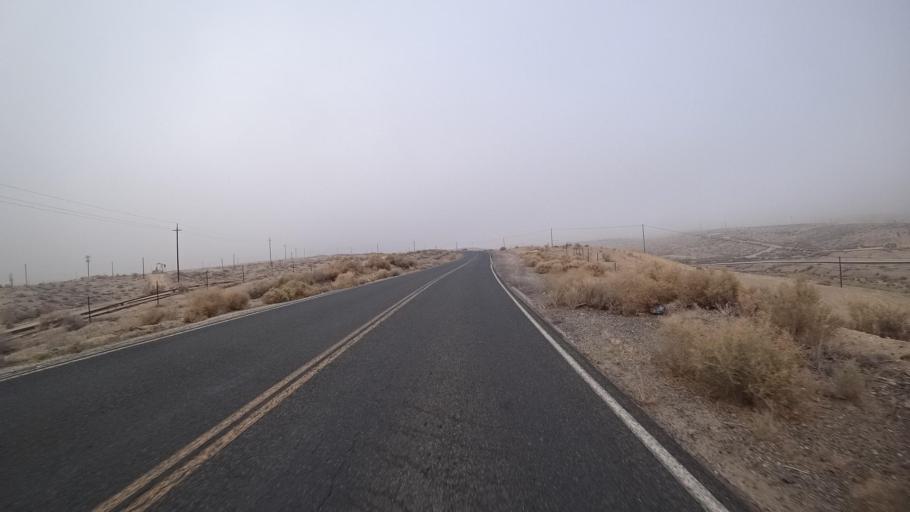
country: US
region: California
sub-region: Kern County
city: Ford City
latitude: 35.2619
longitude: -119.4628
